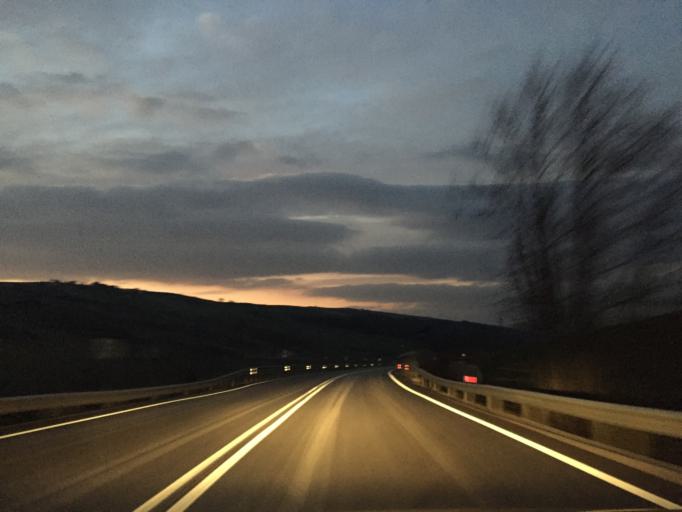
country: IT
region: Apulia
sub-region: Provincia di Foggia
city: Volturara Appula
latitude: 41.4577
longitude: 15.0627
